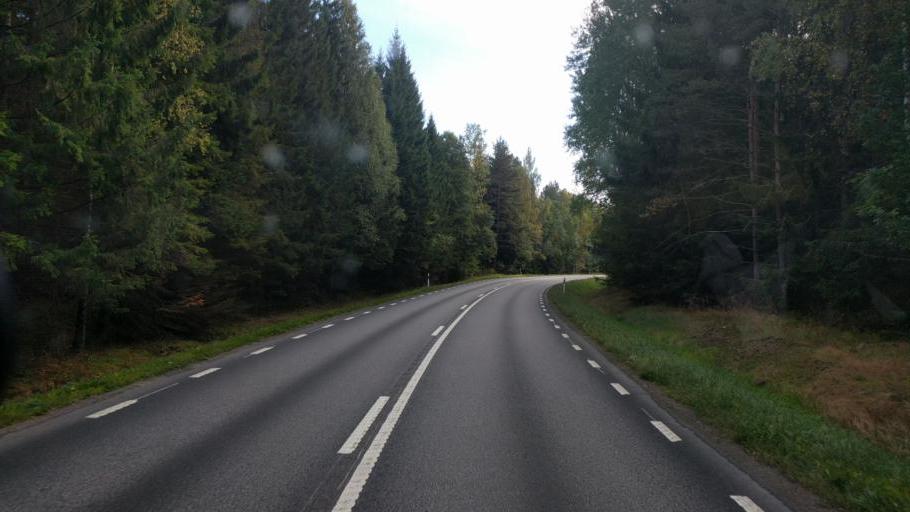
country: SE
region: OEstergoetland
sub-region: Kinda Kommun
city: Kisa
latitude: 57.9643
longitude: 15.6568
